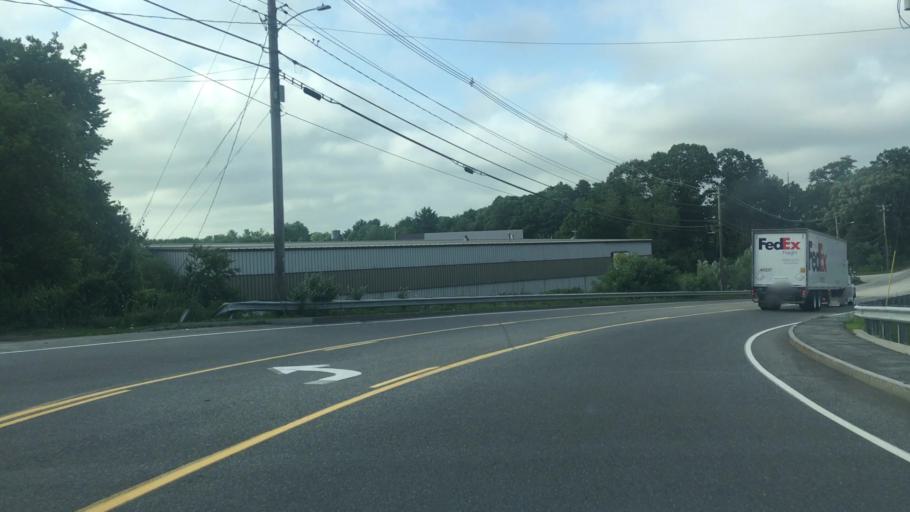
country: US
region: Maine
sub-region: Cumberland County
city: Westbrook
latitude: 43.6870
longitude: -70.3285
